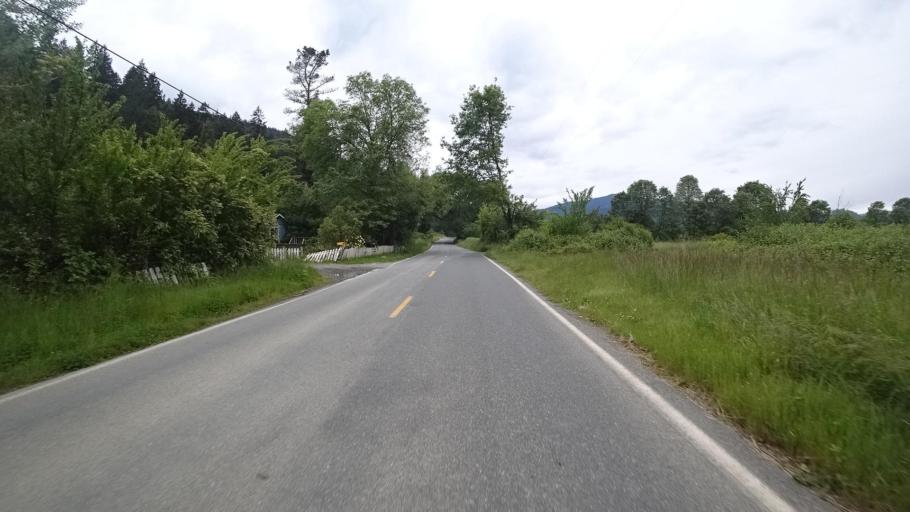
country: US
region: California
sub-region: Humboldt County
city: Willow Creek
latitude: 41.0774
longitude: -123.6968
